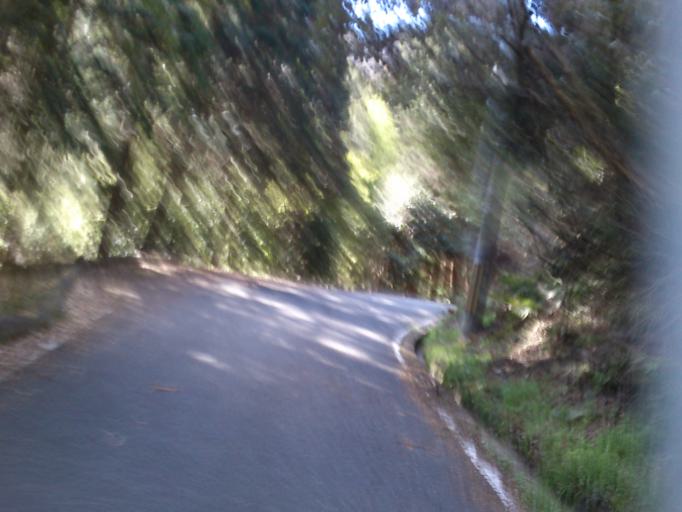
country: JP
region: Kyoto
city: Tanabe
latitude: 34.8004
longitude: 135.8813
